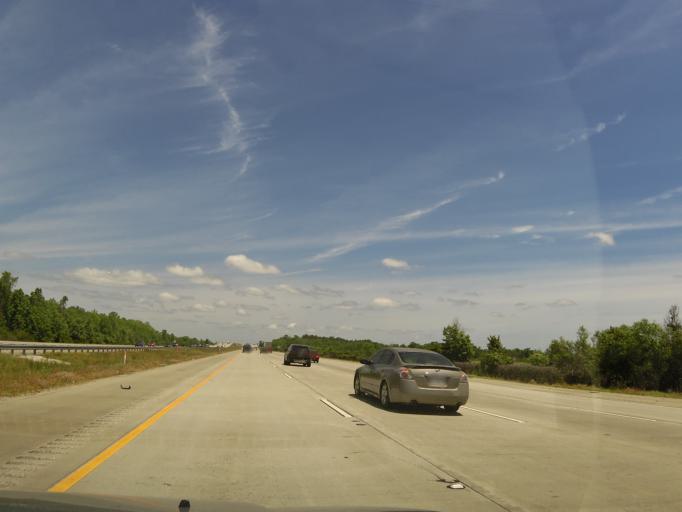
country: US
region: Georgia
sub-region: McIntosh County
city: Darien
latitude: 31.3270
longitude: -81.4715
